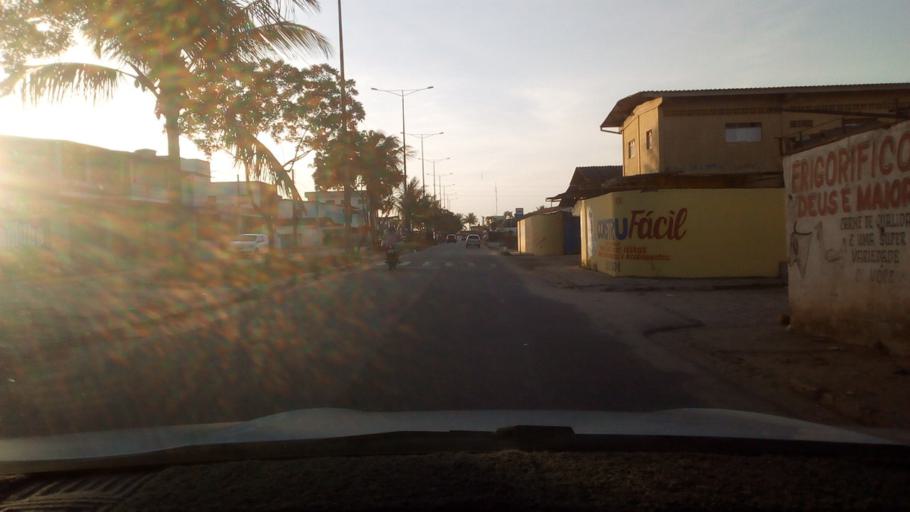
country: BR
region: Paraiba
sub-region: Bayeux
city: Bayeux
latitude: -7.1750
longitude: -34.9279
